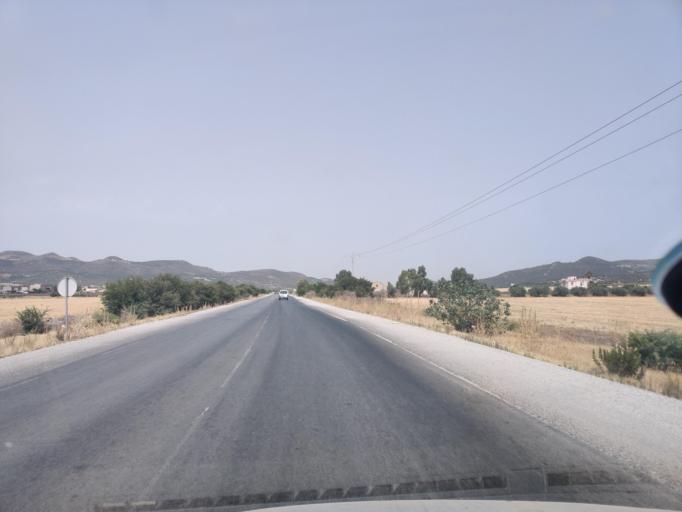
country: TN
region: Tunis
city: Hammam-Lif
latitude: 36.6181
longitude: 10.4155
